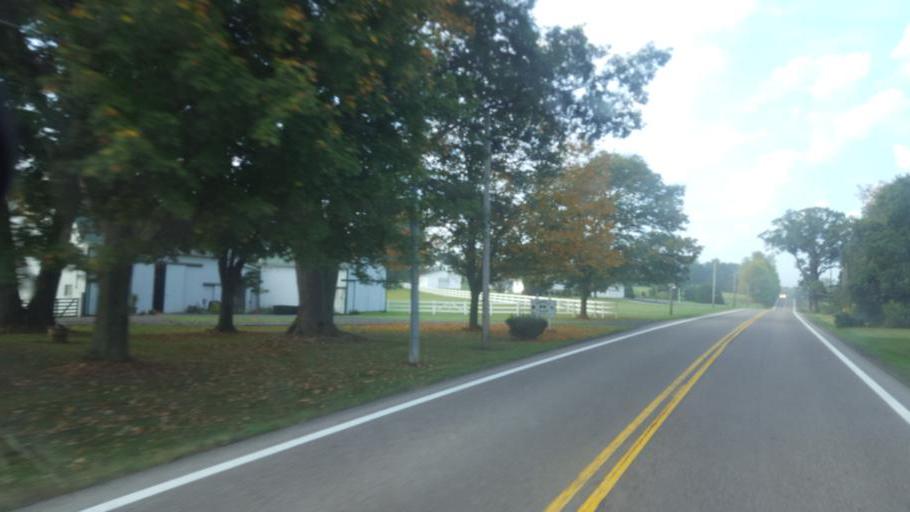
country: US
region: Ohio
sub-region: Knox County
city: Gambier
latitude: 40.2786
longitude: -82.3495
